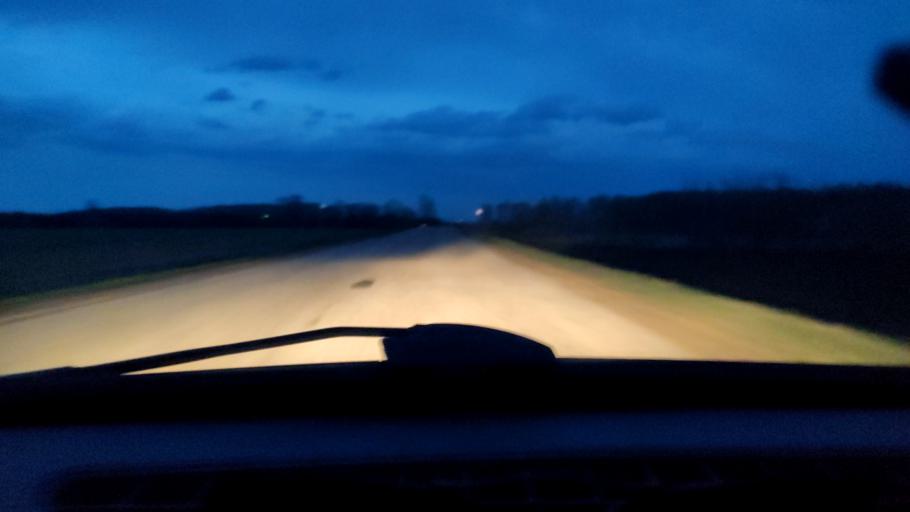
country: RU
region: Bashkortostan
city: Kabakovo
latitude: 54.4770
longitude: 56.1994
